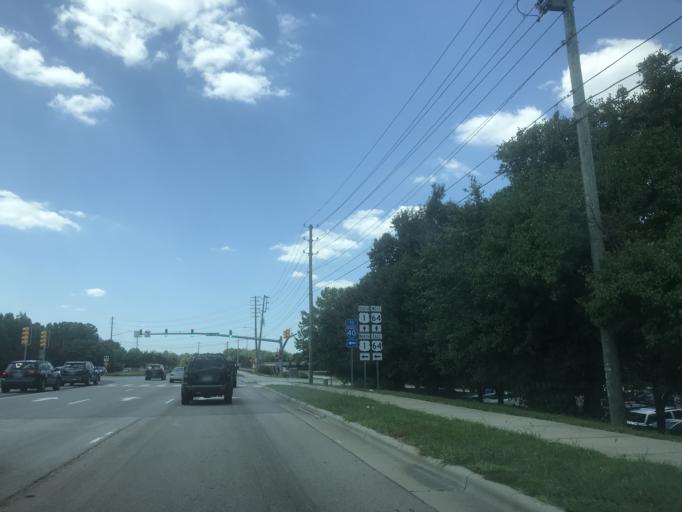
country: US
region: North Carolina
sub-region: Wake County
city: Cary
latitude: 35.7606
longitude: -78.7436
